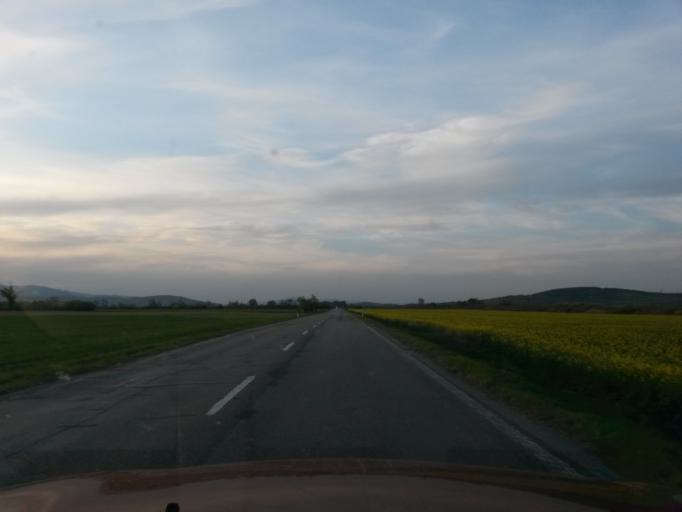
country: HU
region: Borsod-Abauj-Zemplen
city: Satoraljaujhely
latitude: 48.4351
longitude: 21.6571
